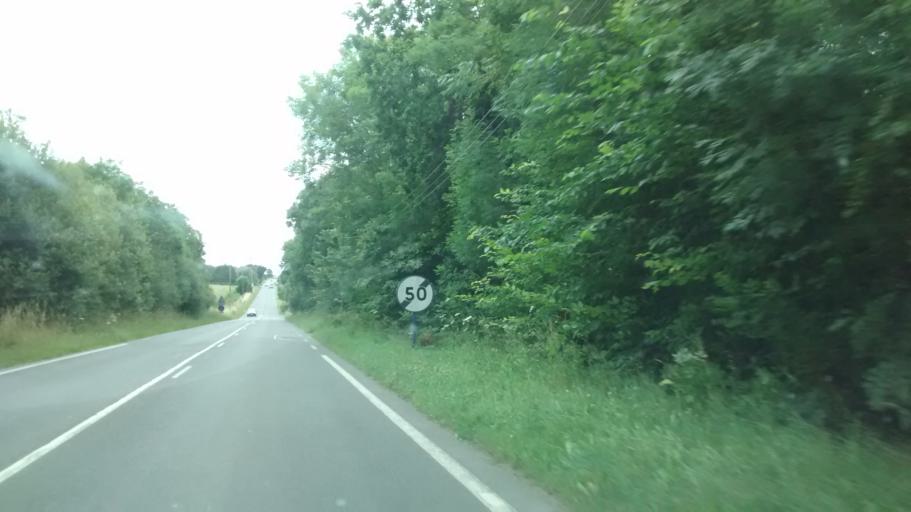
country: FR
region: Brittany
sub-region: Departement d'Ille-et-Vilaine
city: Saint-Meloir-des-Ondes
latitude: 48.6436
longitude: -1.8808
